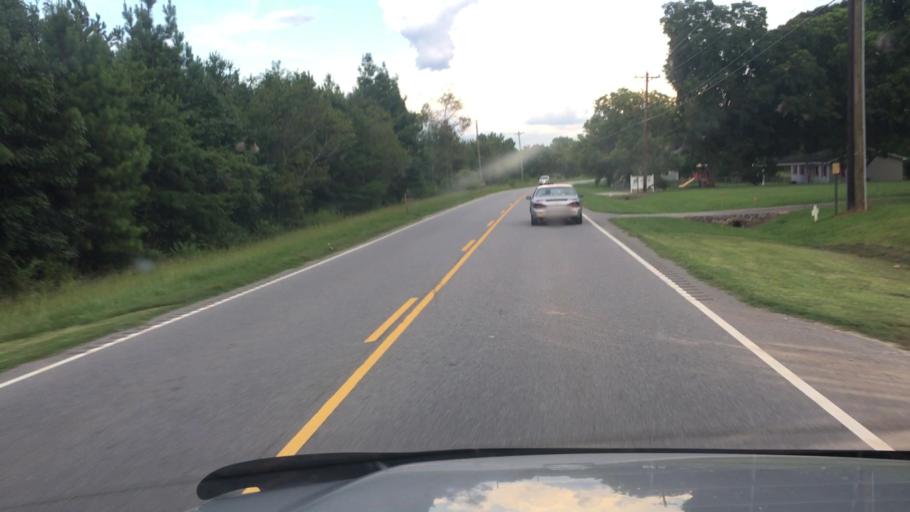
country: US
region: South Carolina
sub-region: Cherokee County
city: Gaffney
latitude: 35.1262
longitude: -81.7313
